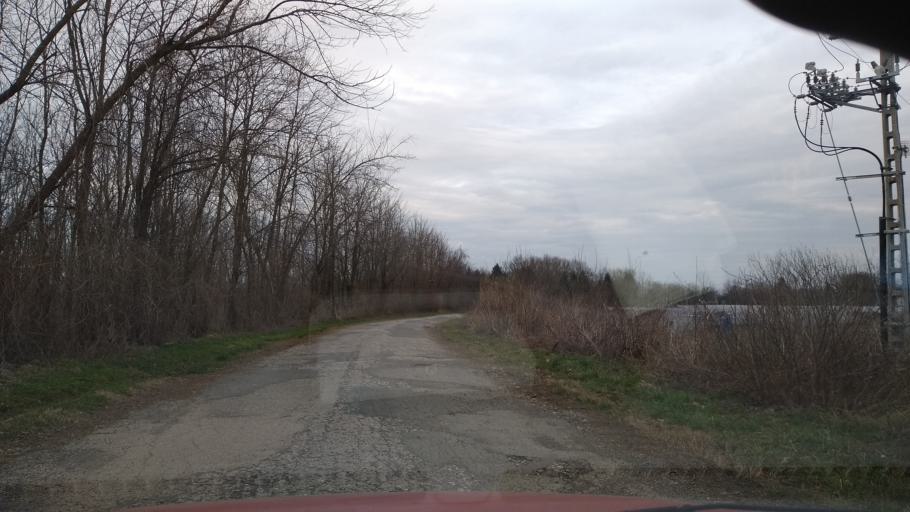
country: HU
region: Somogy
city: Barcs
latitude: 45.9524
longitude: 17.4284
